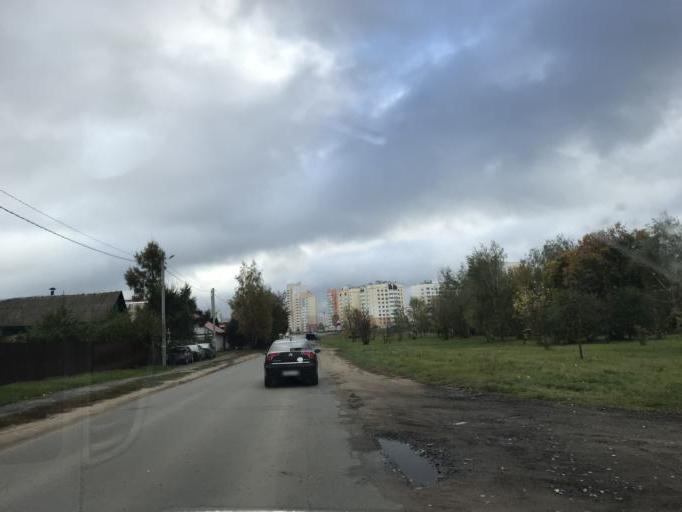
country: BY
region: Mogilev
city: Mahilyow
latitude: 53.8834
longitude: 30.3521
